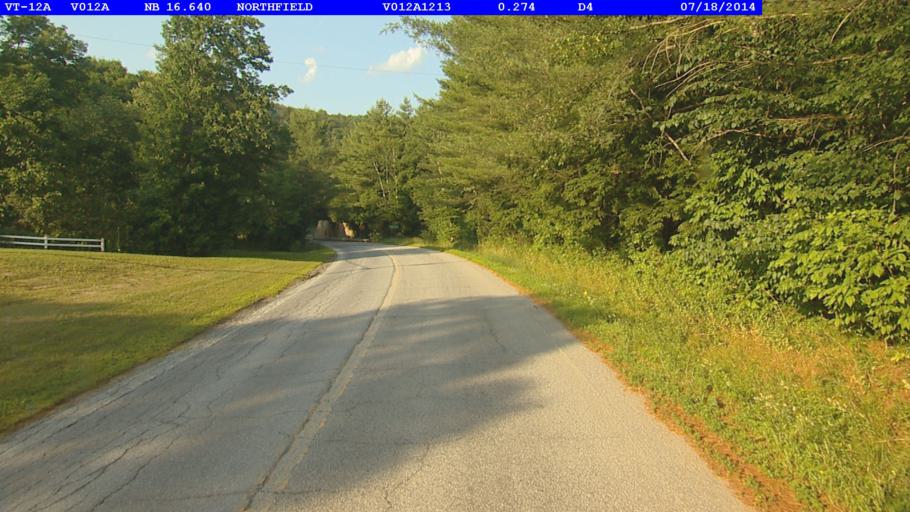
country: US
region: Vermont
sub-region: Washington County
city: Northfield
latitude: 44.1163
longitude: -72.7200
